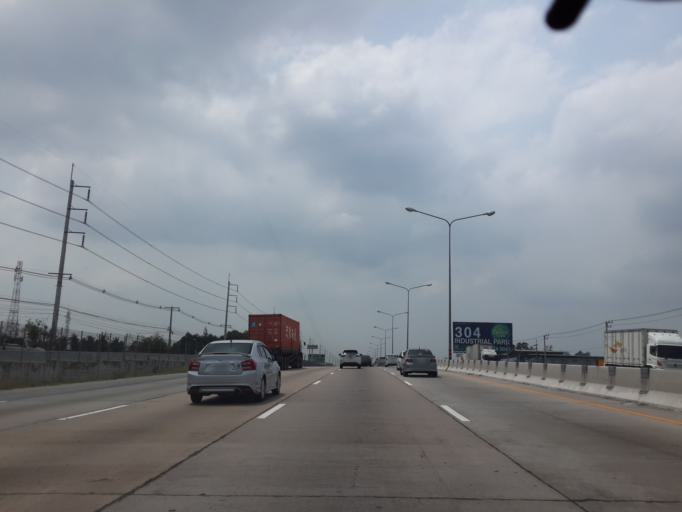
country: TH
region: Chon Buri
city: Si Racha
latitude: 13.1697
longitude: 100.9919
